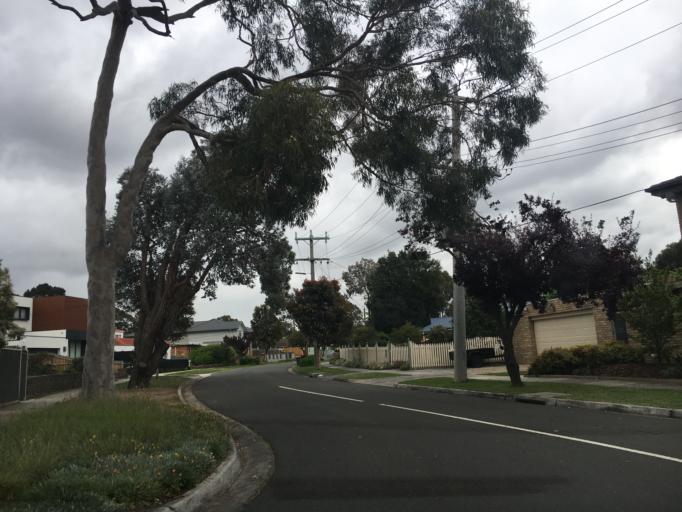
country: AU
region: Victoria
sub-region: Whitehorse
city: Vermont South
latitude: -37.8715
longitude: 145.1790
